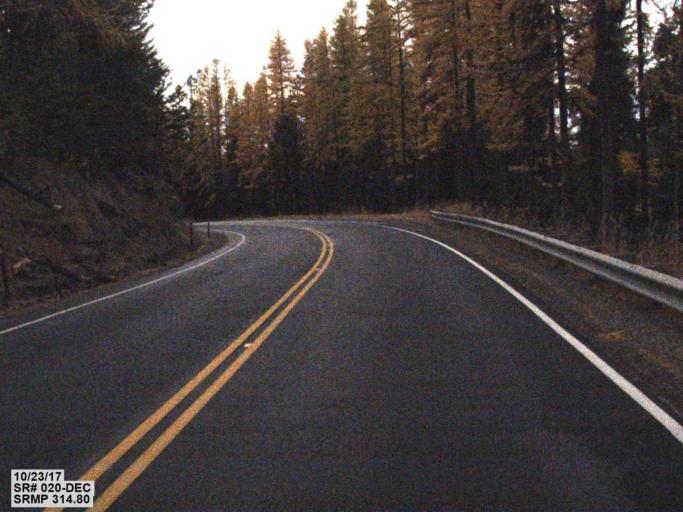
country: US
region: Washington
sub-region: Ferry County
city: Republic
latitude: 48.6125
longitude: -118.5473
